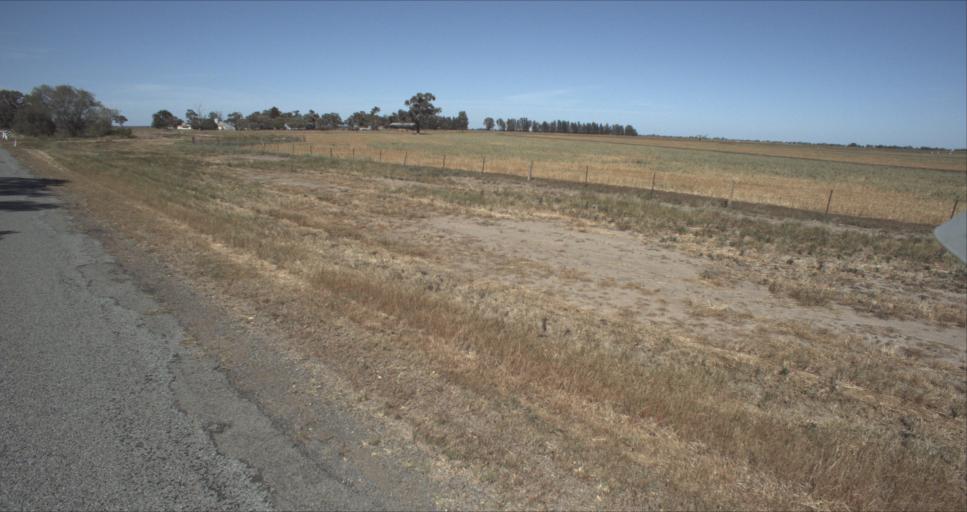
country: AU
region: New South Wales
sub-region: Leeton
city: Leeton
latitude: -34.5388
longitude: 146.3169
